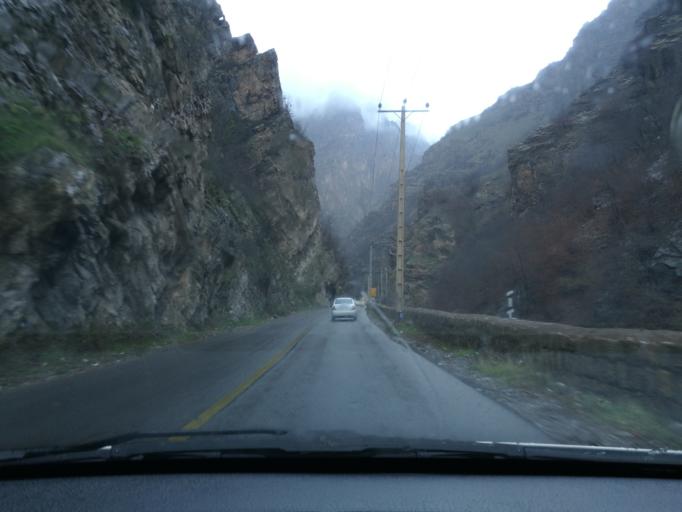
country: IR
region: Mazandaran
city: Chalus
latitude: 36.2678
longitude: 51.2535
